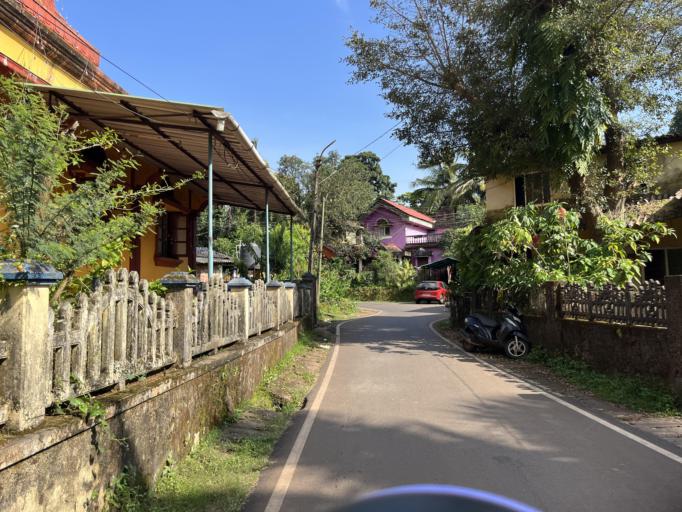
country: IN
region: Goa
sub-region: North Goa
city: Ponda
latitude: 15.3977
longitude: 74.0130
